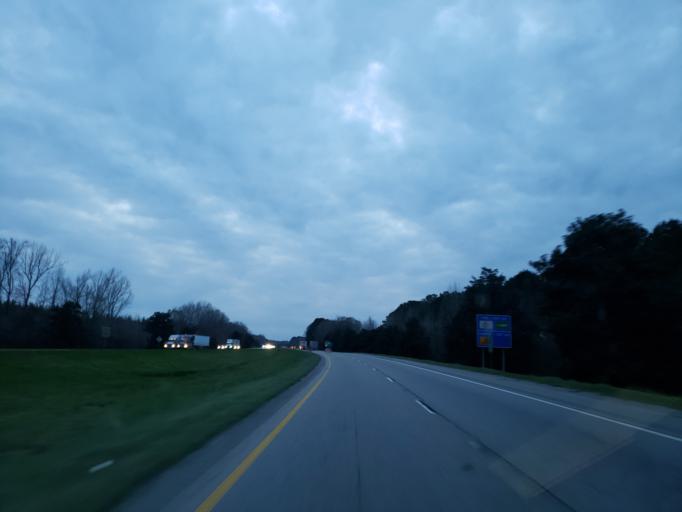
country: US
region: Mississippi
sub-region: Lauderdale County
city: Marion
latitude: 32.4135
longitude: -88.4947
